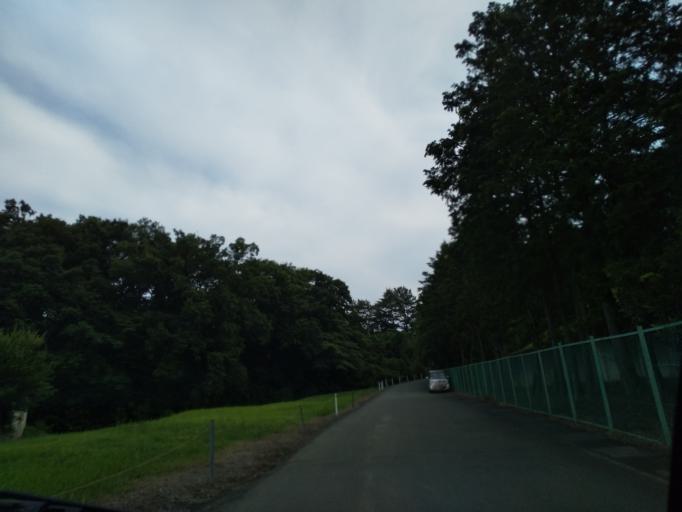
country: JP
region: Kanagawa
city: Atsugi
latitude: 35.4820
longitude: 139.3275
